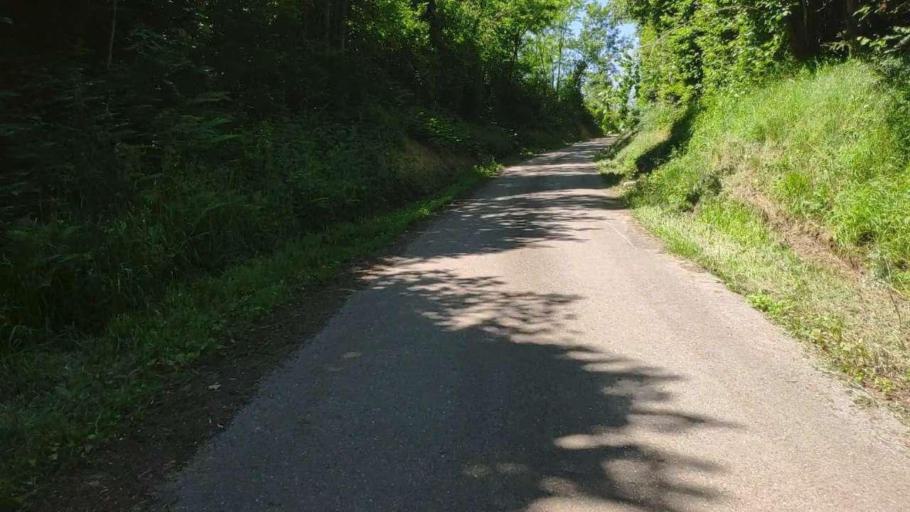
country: FR
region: Franche-Comte
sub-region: Departement du Jura
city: Bletterans
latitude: 46.7478
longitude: 5.3963
